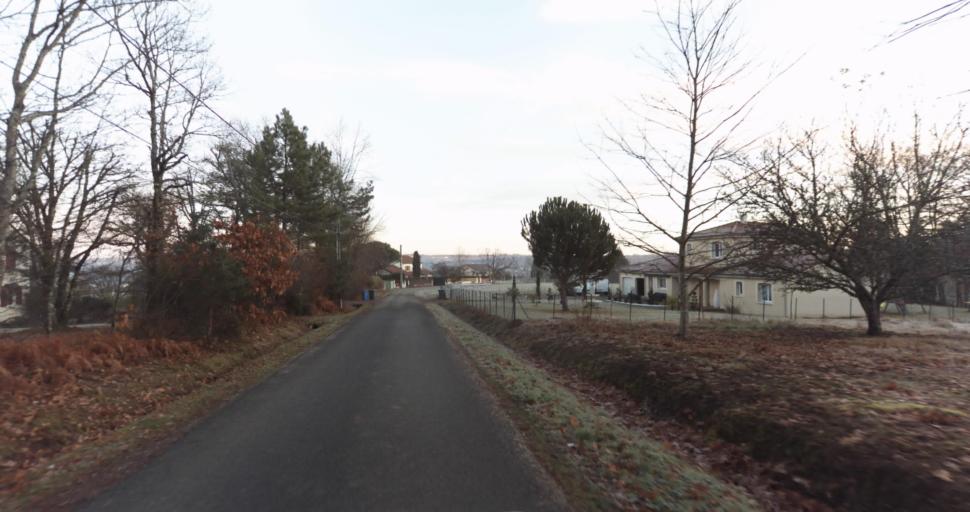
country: FR
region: Limousin
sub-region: Departement de la Haute-Vienne
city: Aixe-sur-Vienne
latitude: 45.8175
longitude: 1.1617
